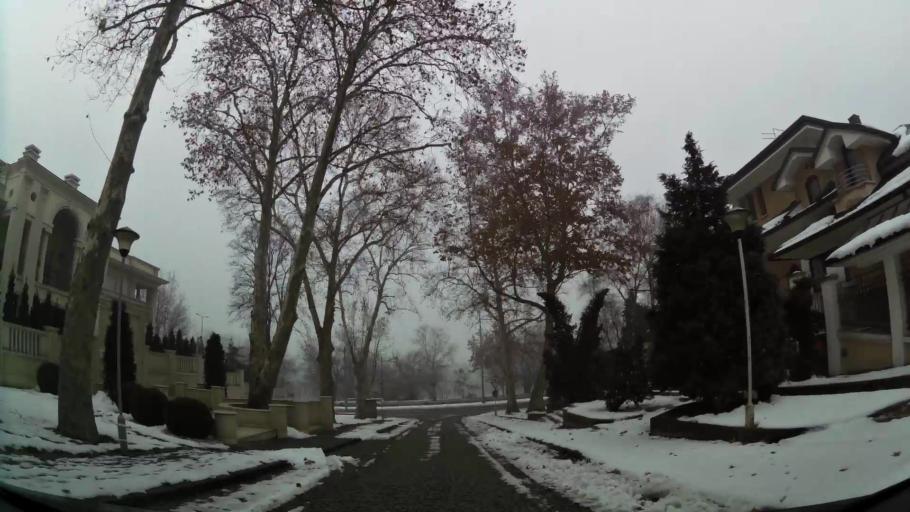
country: RS
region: Central Serbia
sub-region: Belgrade
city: Savski Venac
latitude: 44.7884
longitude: 20.4550
